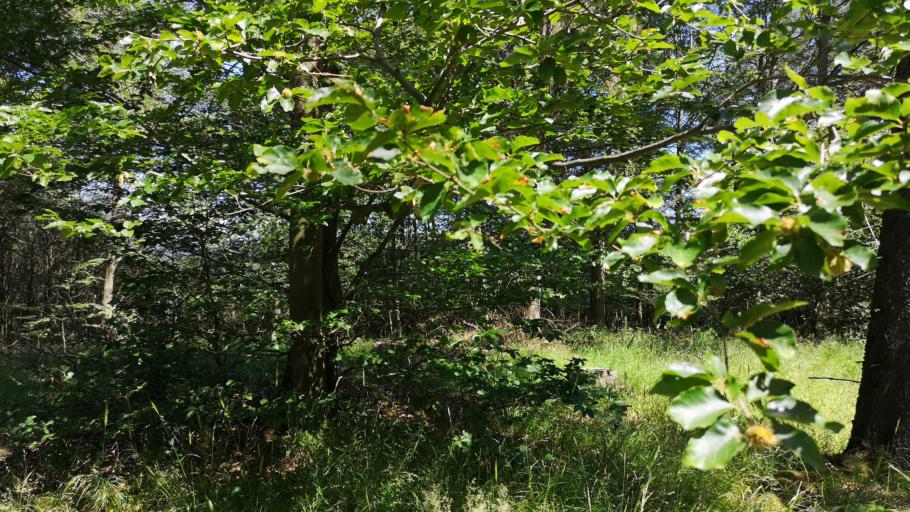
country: DE
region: Saxony-Anhalt
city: Stolberg
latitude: 51.5509
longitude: 10.9668
